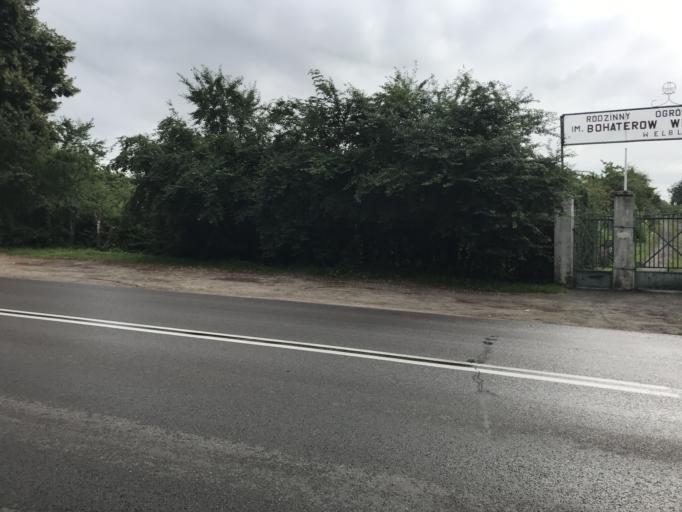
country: PL
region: Warmian-Masurian Voivodeship
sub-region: Powiat elblaski
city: Elblag
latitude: 54.1718
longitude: 19.4243
